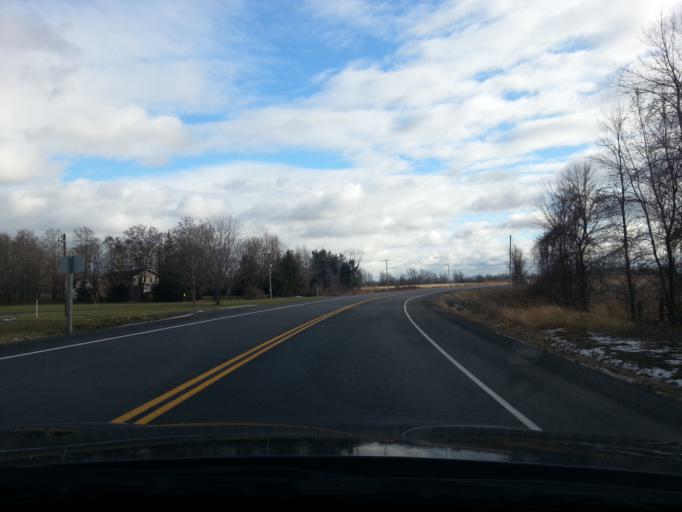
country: CA
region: Ontario
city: Prescott
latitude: 45.0588
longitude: -75.5158
